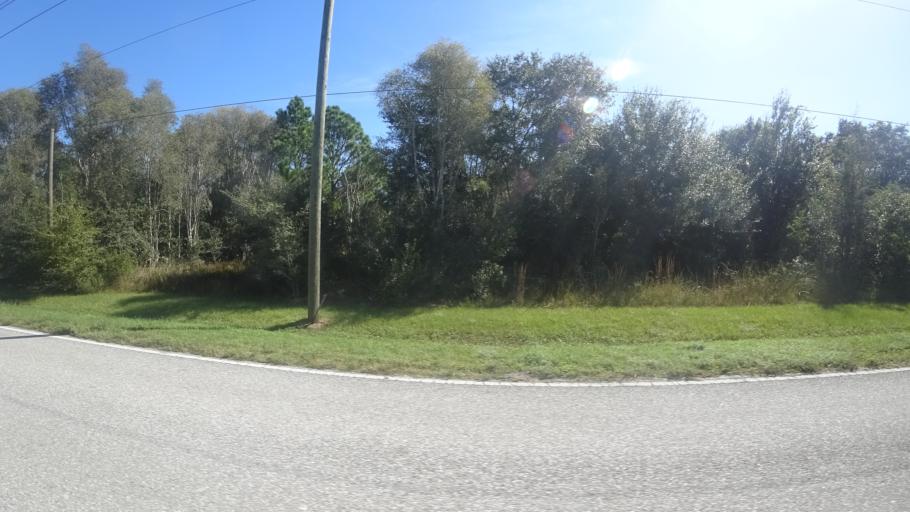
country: US
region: Florida
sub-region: Sarasota County
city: Lake Sarasota
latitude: 27.3808
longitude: -82.2683
